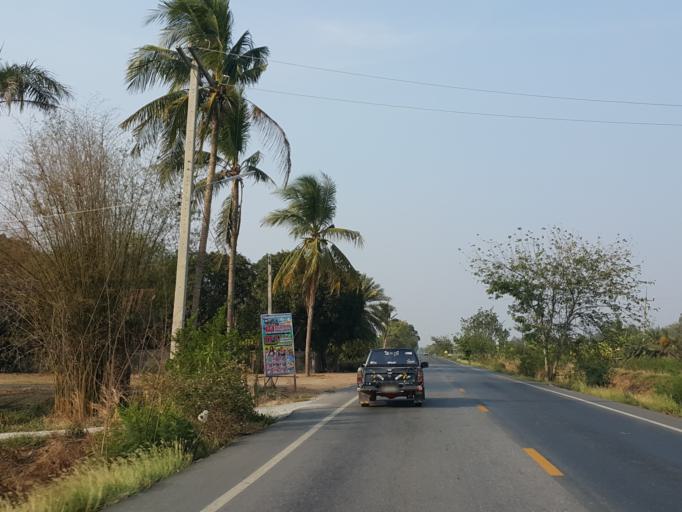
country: TH
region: Chai Nat
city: Sankhaburi
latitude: 14.9860
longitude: 100.1103
